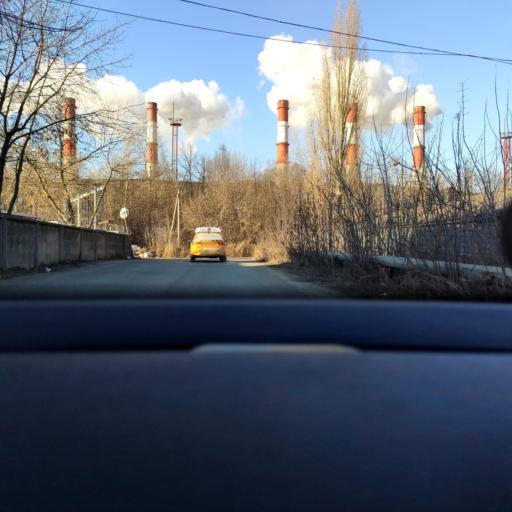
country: RU
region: Moskovskaya
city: Kotel'niki
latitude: 55.6313
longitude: 37.8234
